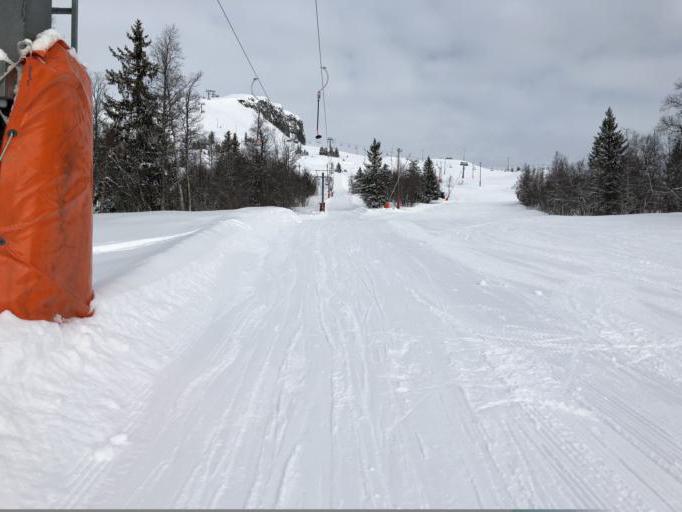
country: NO
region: Oppland
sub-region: Gausdal
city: Segalstad bru
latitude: 61.3405
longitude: 10.0868
